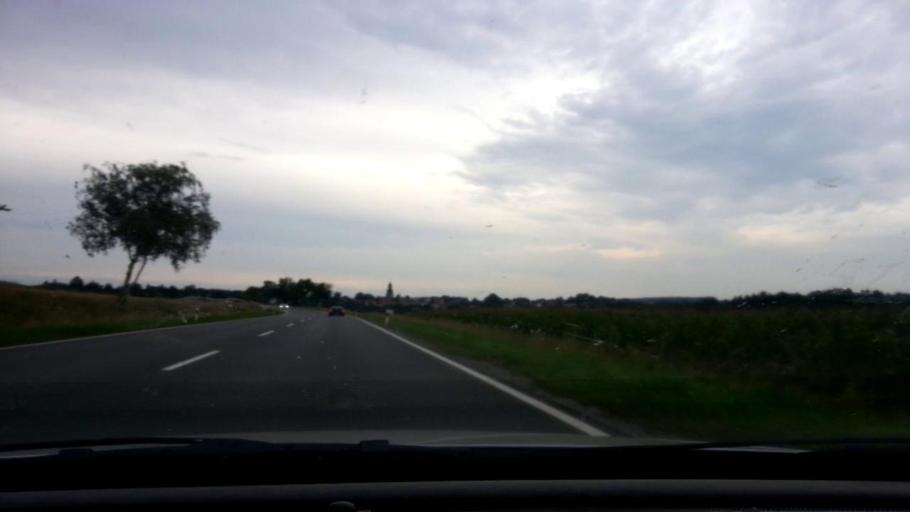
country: DE
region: Bavaria
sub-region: Upper Franconia
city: Neunkirchen am Main
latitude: 49.9148
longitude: 11.6539
